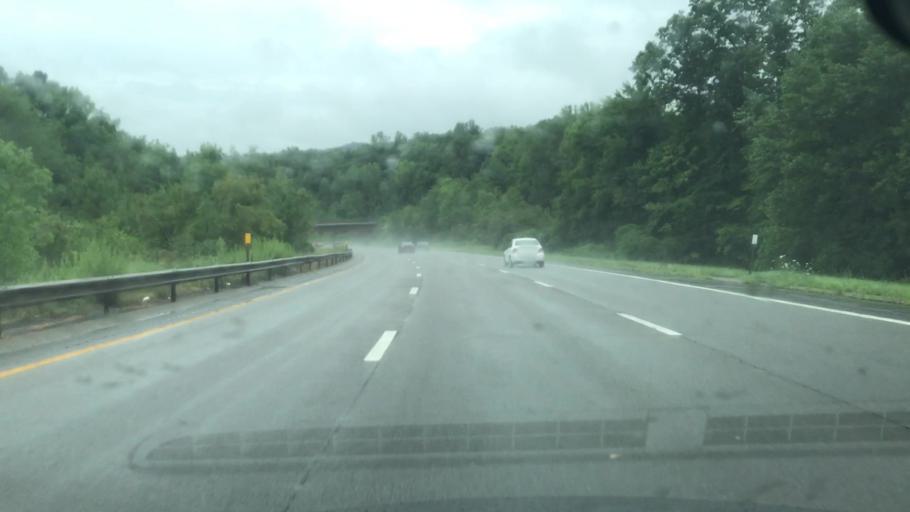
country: US
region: New York
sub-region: Westchester County
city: Yorktown Heights
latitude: 41.2255
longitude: -73.8072
